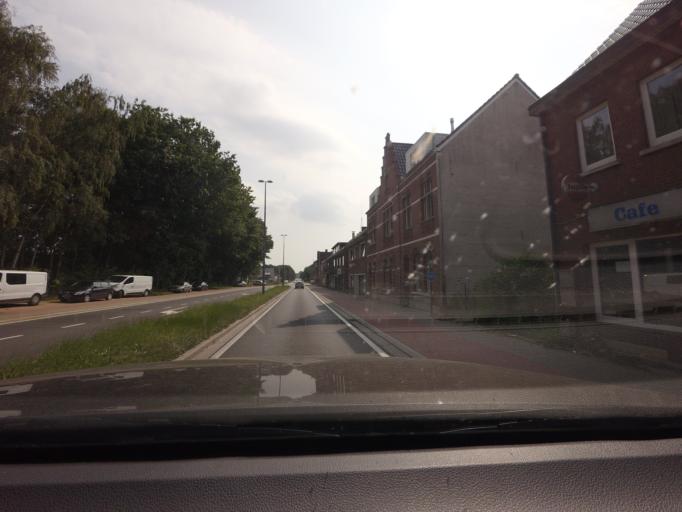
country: BE
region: Flanders
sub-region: Provincie Limburg
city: Beringen
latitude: 51.0860
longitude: 5.2189
